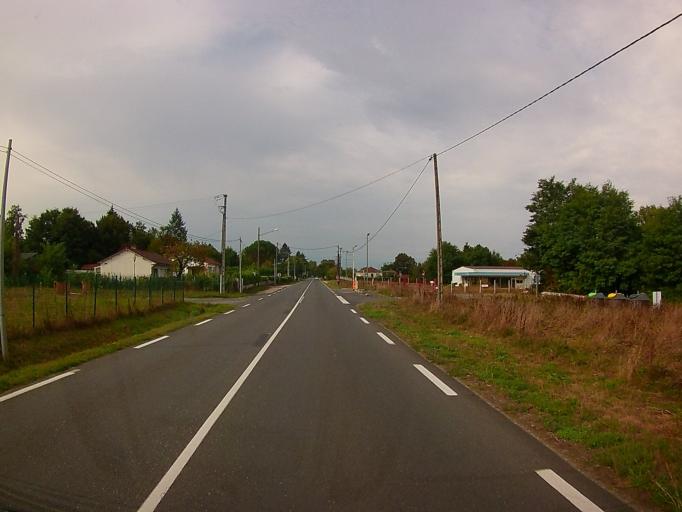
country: FR
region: Aquitaine
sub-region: Departement de la Dordogne
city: Annesse-et-Beaulieu
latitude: 45.1771
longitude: 0.6173
